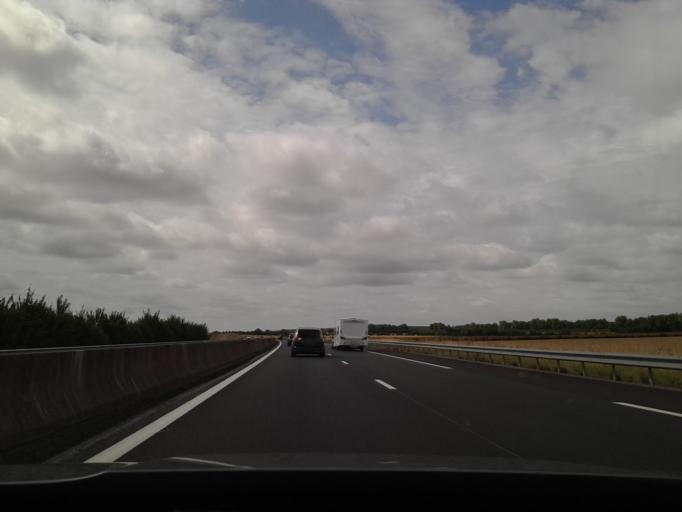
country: FR
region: Lower Normandy
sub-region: Departement de l'Orne
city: Sees
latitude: 48.5791
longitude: 0.1770
